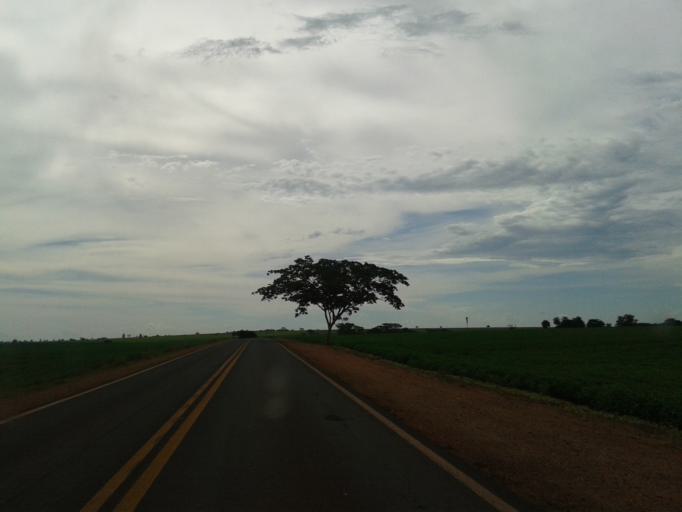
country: BR
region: Minas Gerais
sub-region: Capinopolis
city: Capinopolis
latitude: -18.6929
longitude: -49.4780
